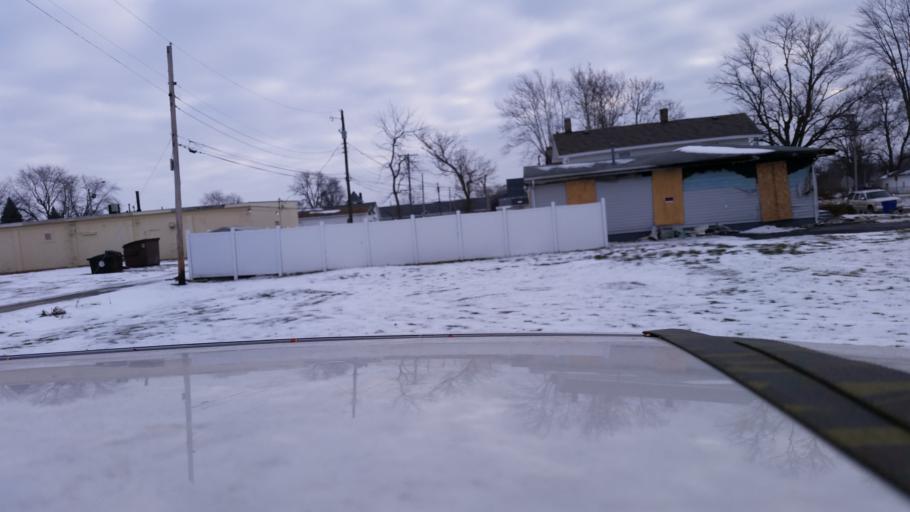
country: US
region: Indiana
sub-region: Howard County
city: Kokomo
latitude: 40.4938
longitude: -86.1292
